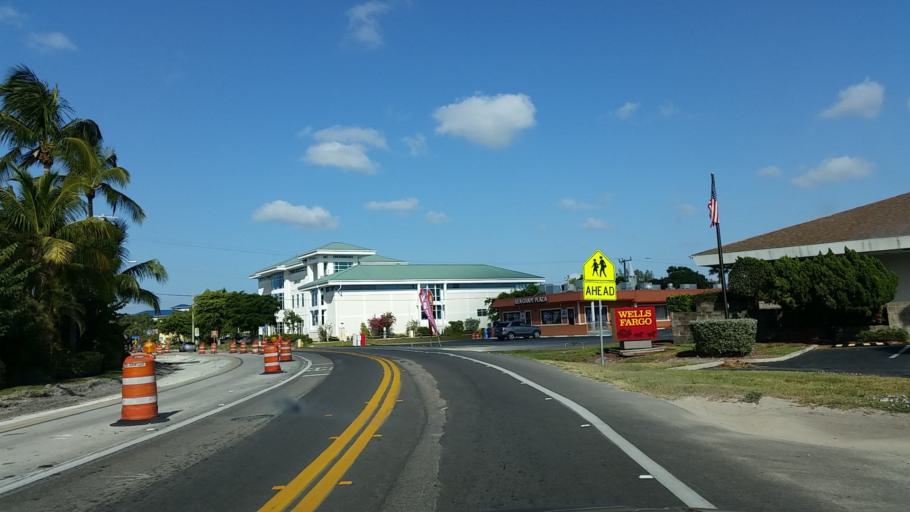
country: US
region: Florida
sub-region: Lee County
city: Fort Myers Beach
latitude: 26.4468
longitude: -81.9381
